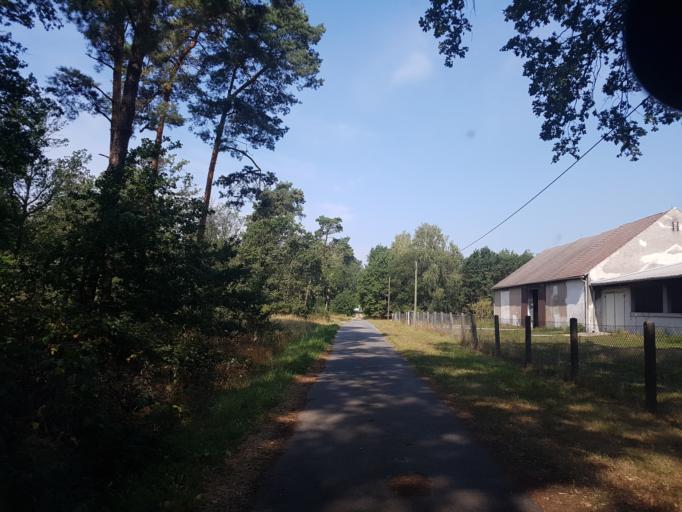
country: DE
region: Brandenburg
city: Sonnewalde
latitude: 51.6859
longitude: 13.6933
